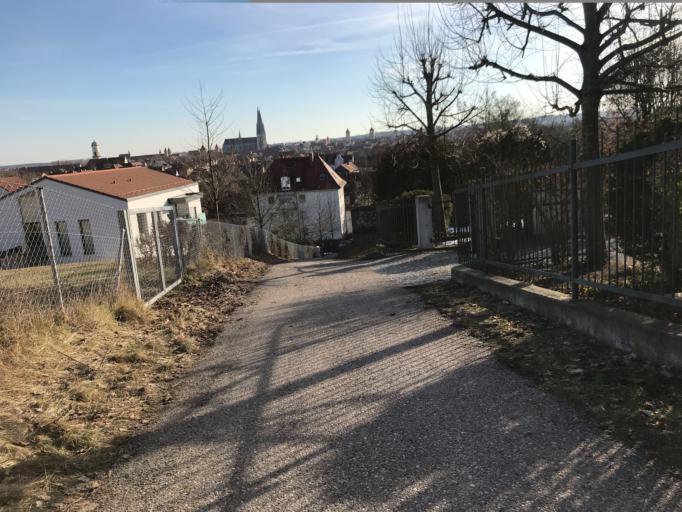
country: DE
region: Bavaria
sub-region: Upper Palatinate
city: Lappersdorf
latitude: 49.0303
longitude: 12.0956
